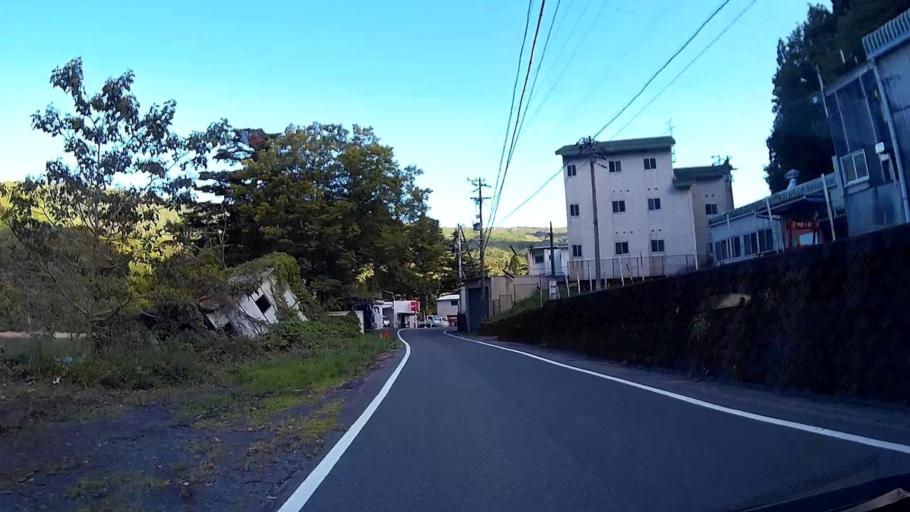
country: JP
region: Shizuoka
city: Shizuoka-shi
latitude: 35.2251
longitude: 138.2437
